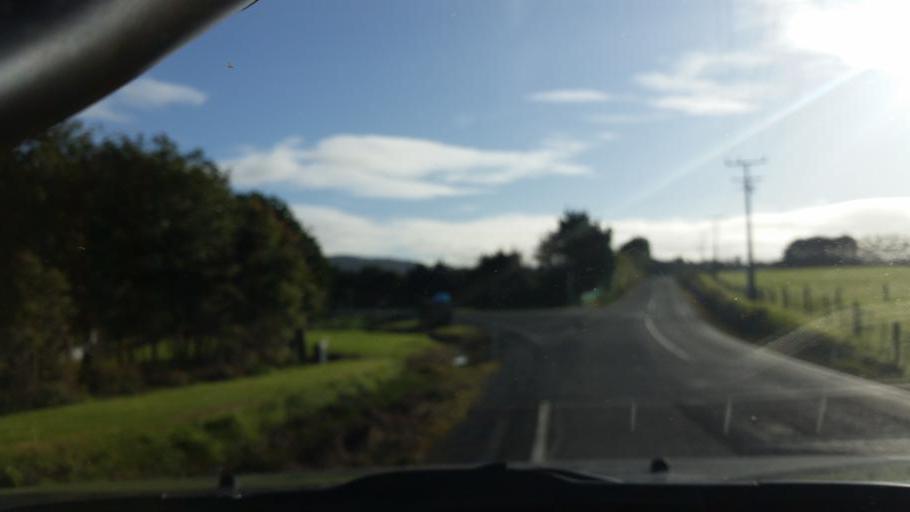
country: NZ
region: Auckland
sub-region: Auckland
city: Wellsford
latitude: -36.1071
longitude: 174.5531
